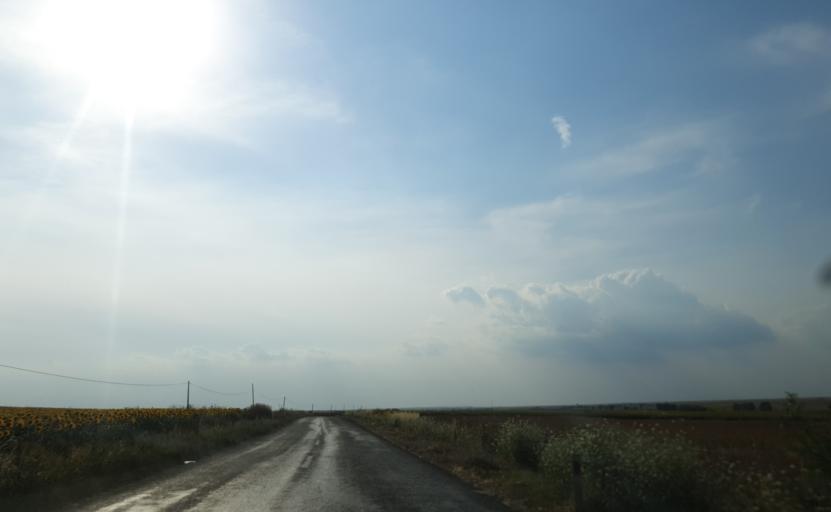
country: TR
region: Tekirdag
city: Muratli
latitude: 41.2105
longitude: 27.4501
